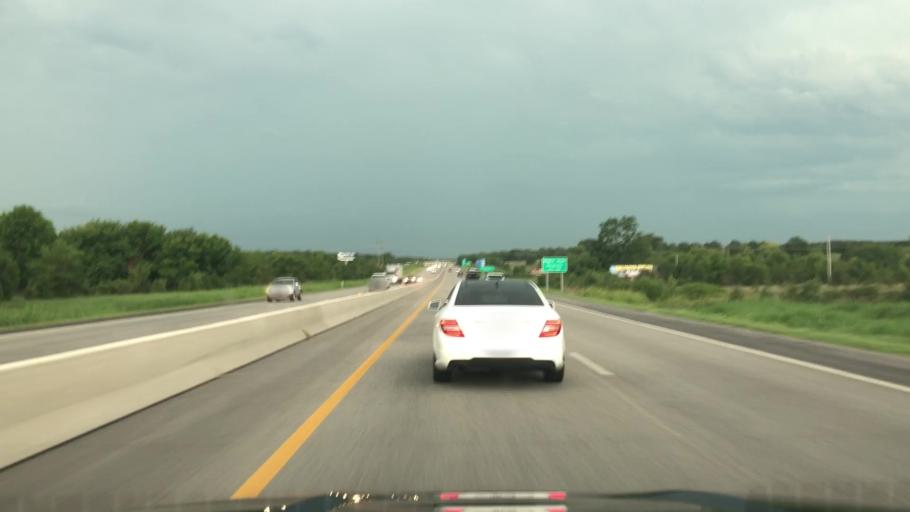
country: US
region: Oklahoma
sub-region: Rogers County
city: Justice
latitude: 36.3126
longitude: -95.5654
